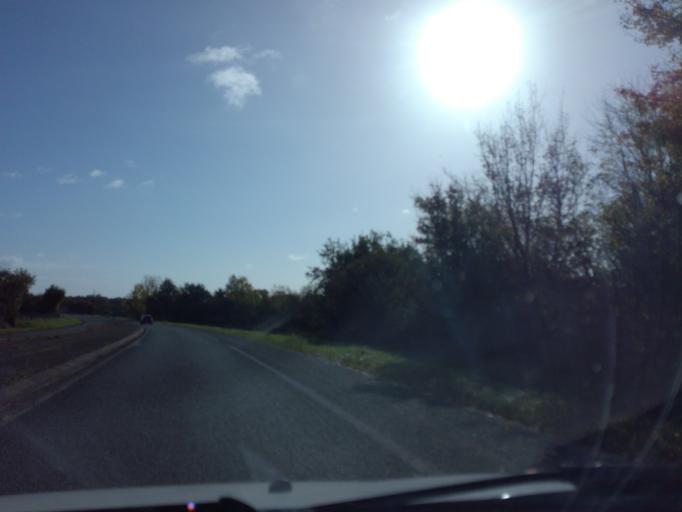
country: FR
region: Pays de la Loire
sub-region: Departement de Maine-et-Loire
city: Pouance
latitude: 47.7762
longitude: -1.2399
